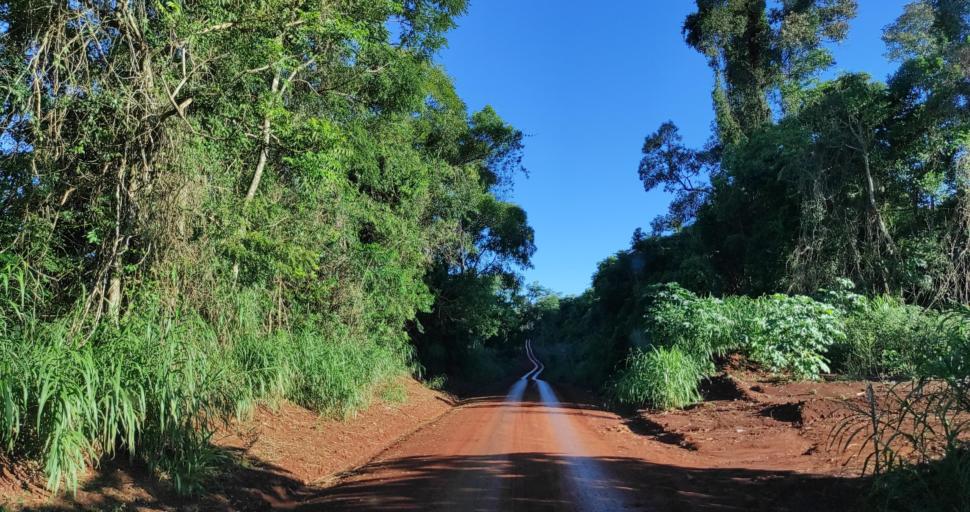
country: AR
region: Misiones
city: Puerto Rico
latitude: -26.8321
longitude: -55.0118
